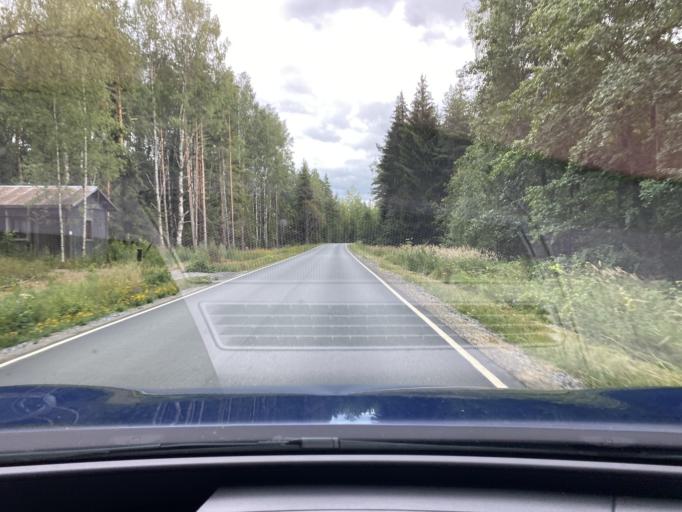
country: FI
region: Pirkanmaa
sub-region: Lounais-Pirkanmaa
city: Vammala
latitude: 61.3011
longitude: 22.9611
